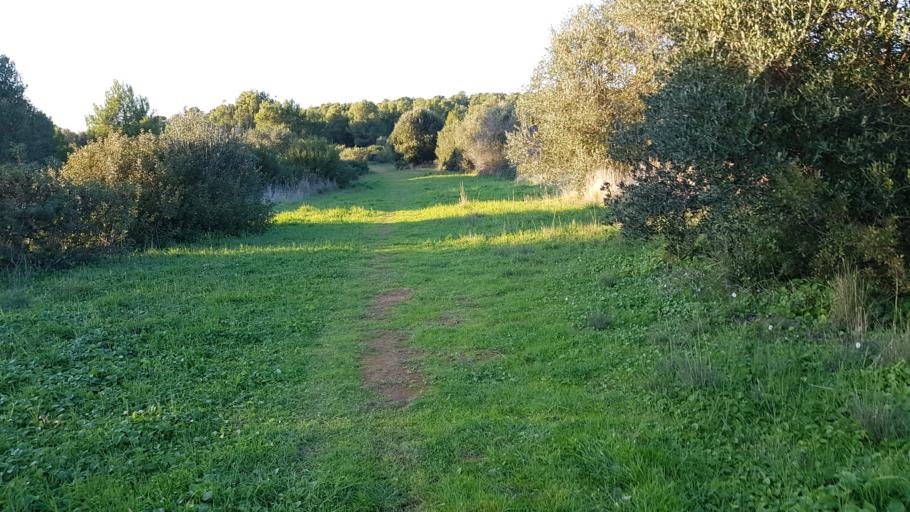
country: IT
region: Apulia
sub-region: Provincia di Lecce
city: Nardo
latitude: 40.1519
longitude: 17.9649
